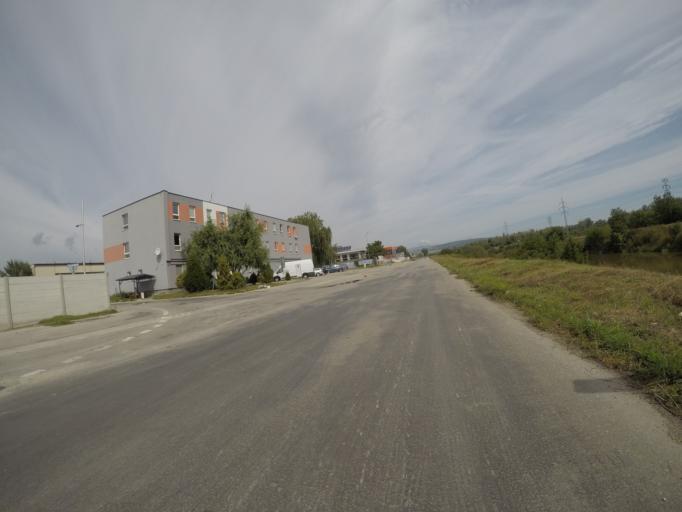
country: SK
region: Trenciansky
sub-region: Okres Nove Mesto nad Vahom
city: Nove Mesto nad Vahom
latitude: 48.7480
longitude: 17.8455
